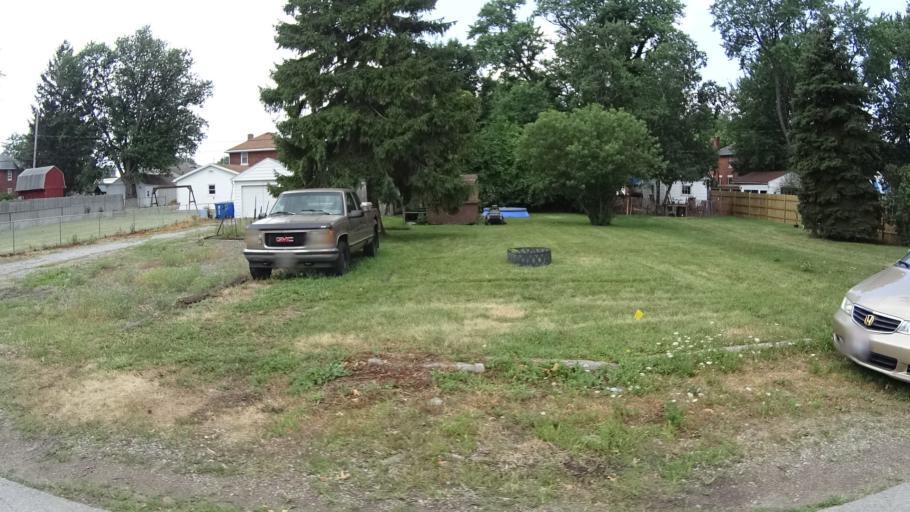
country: US
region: Ohio
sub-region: Erie County
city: Sandusky
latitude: 41.4469
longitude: -82.7409
